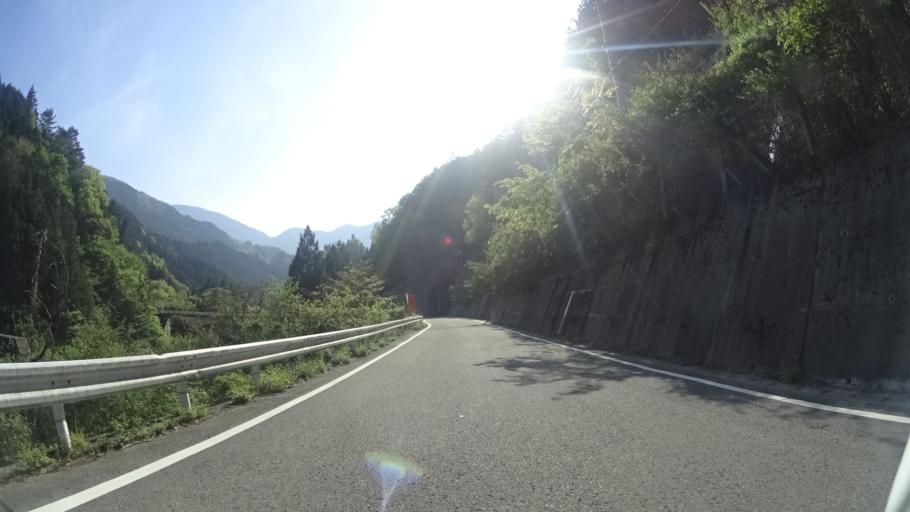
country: JP
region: Tokushima
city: Ikedacho
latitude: 33.8666
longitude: 133.9628
